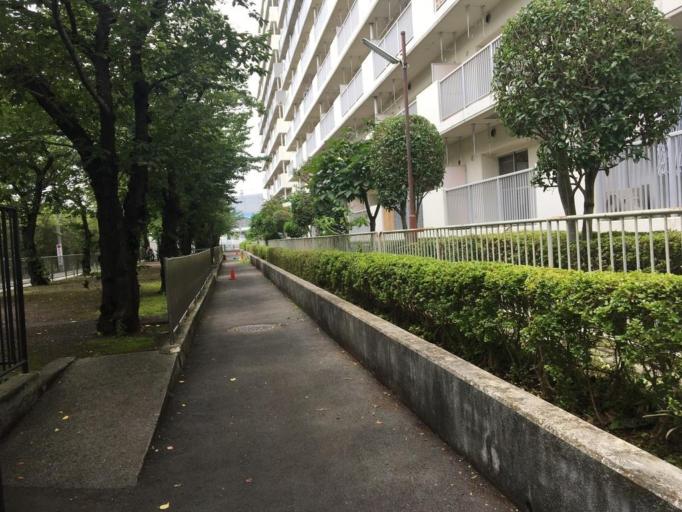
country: JP
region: Saitama
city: Shimotoda
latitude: 35.8073
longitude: 139.6583
